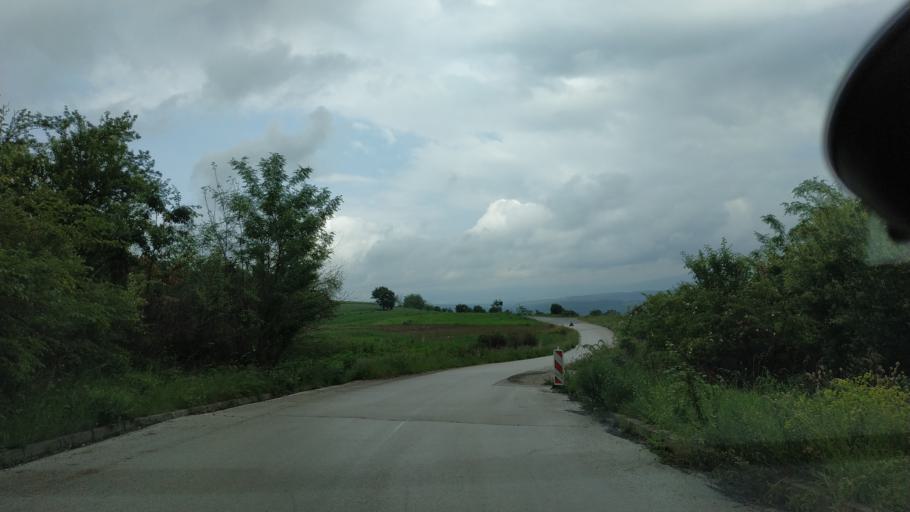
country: RS
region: Central Serbia
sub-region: Toplicki Okrug
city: Prokuplje
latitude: 43.4166
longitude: 21.5535
